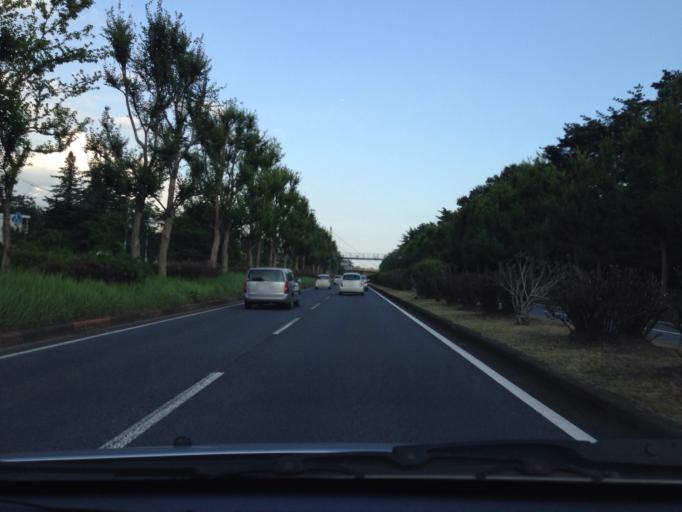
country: JP
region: Ibaraki
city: Naka
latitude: 36.0635
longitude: 140.1379
